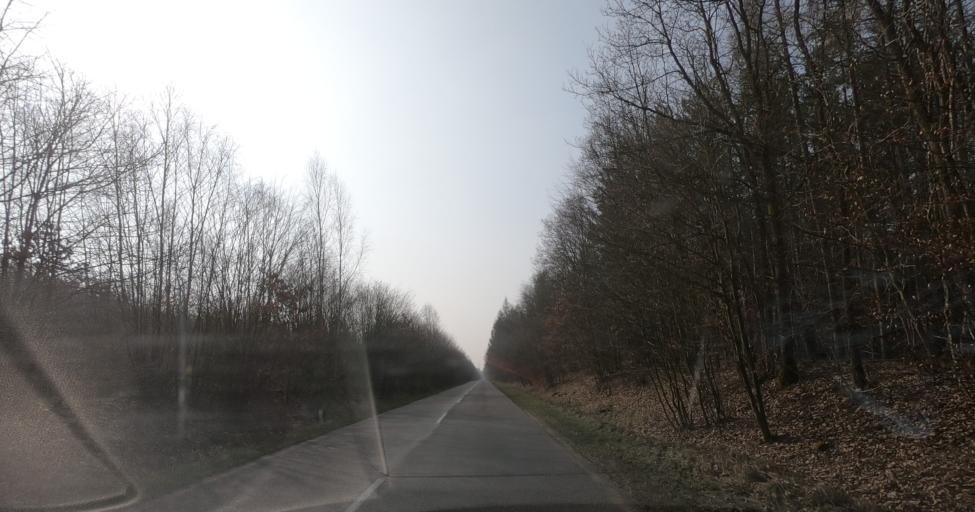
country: PL
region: West Pomeranian Voivodeship
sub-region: Powiat gryfinski
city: Banie
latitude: 53.0042
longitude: 14.7233
